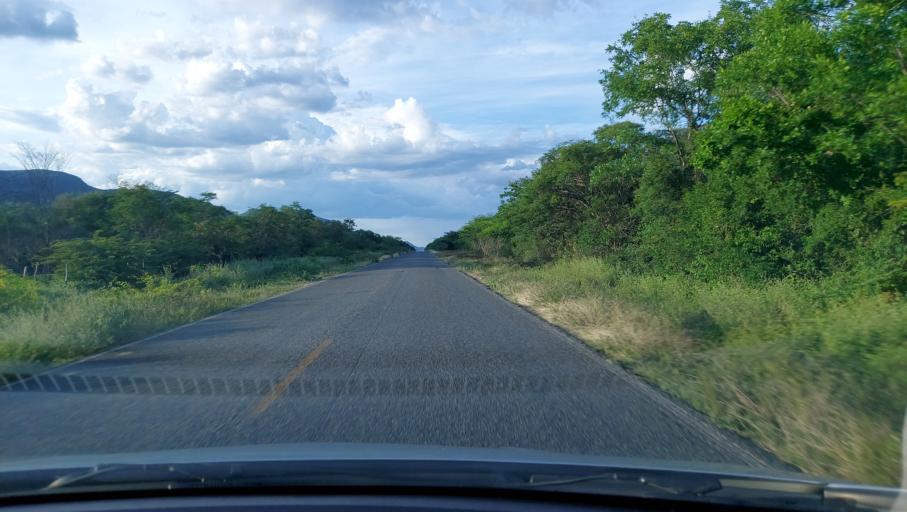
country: BR
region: Bahia
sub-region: Oliveira Dos Brejinhos
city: Beira Rio
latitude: -12.1851
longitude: -42.5402
